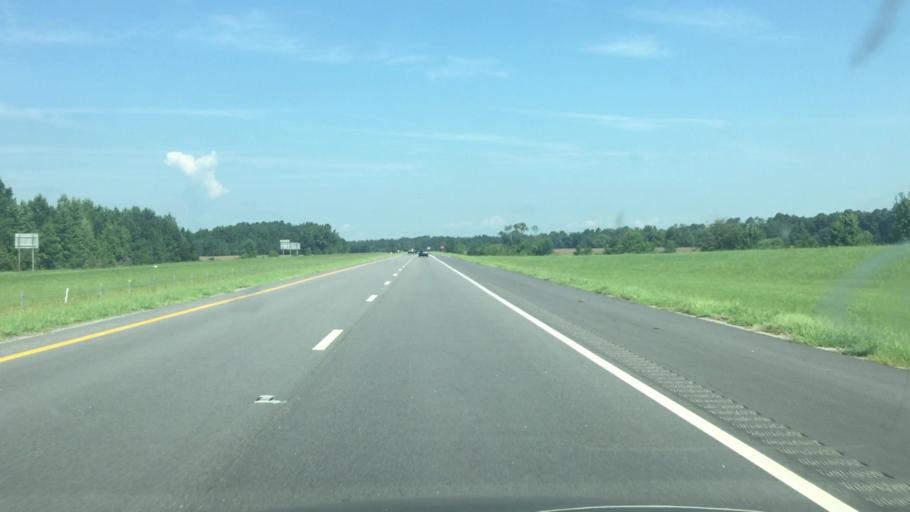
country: US
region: North Carolina
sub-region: Robeson County
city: Pembroke
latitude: 34.6843
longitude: -79.2770
